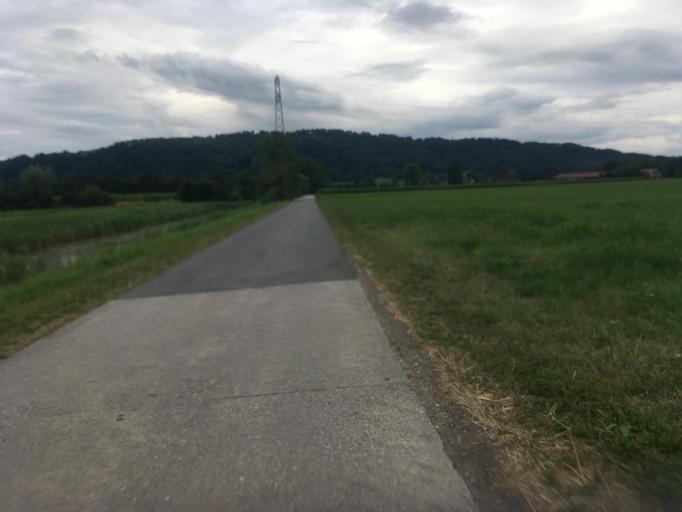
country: CH
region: Fribourg
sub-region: See District
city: Bas-Vully
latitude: 46.9826
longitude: 7.1022
